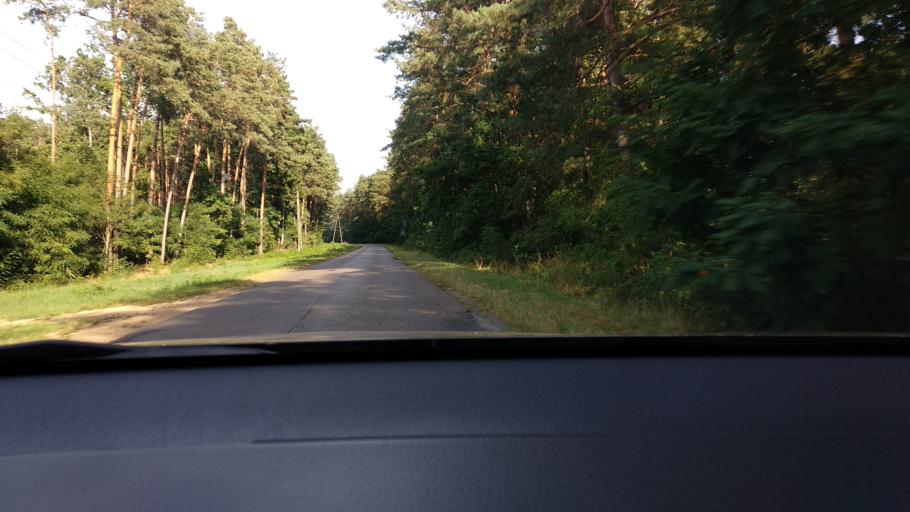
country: PL
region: Masovian Voivodeship
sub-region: Powiat pultuski
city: Pultusk
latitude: 52.7129
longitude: 21.1570
